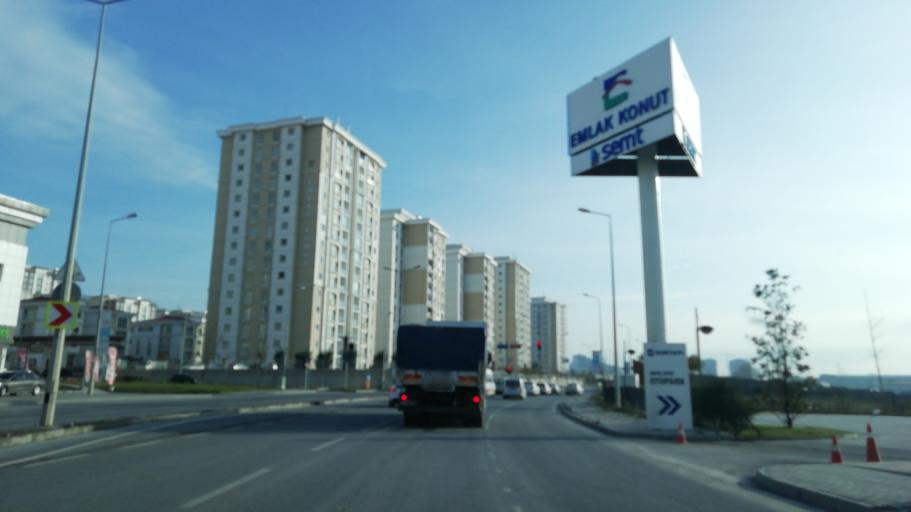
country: TR
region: Istanbul
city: Esenyurt
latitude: 41.0864
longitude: 28.6513
